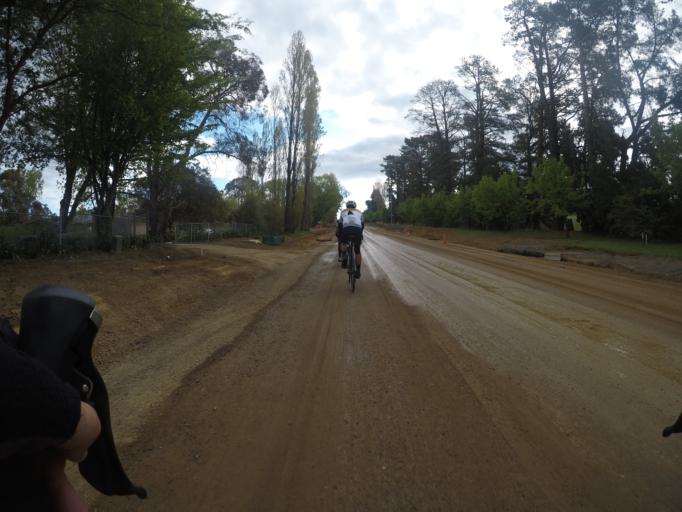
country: AU
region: New South Wales
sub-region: Orange Municipality
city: Orange
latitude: -33.2844
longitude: 149.0640
